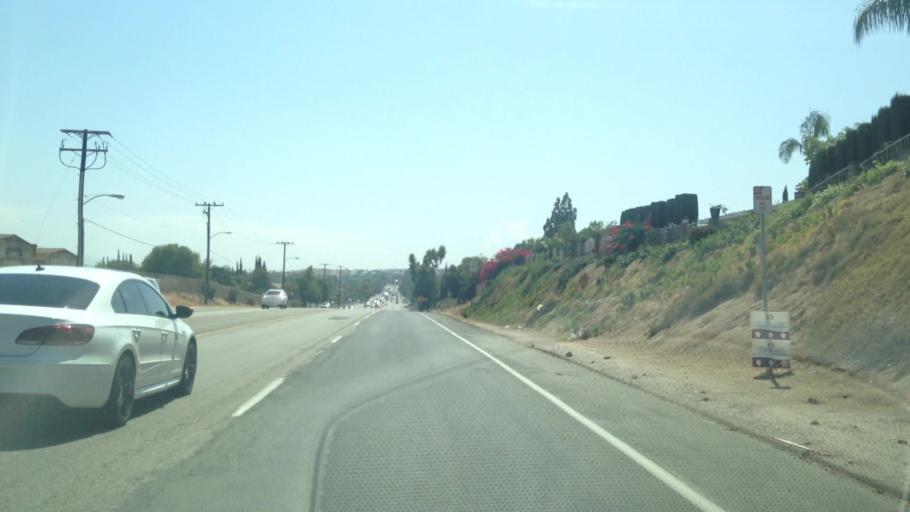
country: US
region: California
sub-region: Riverside County
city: Woodcrest
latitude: 33.8823
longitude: -117.3746
